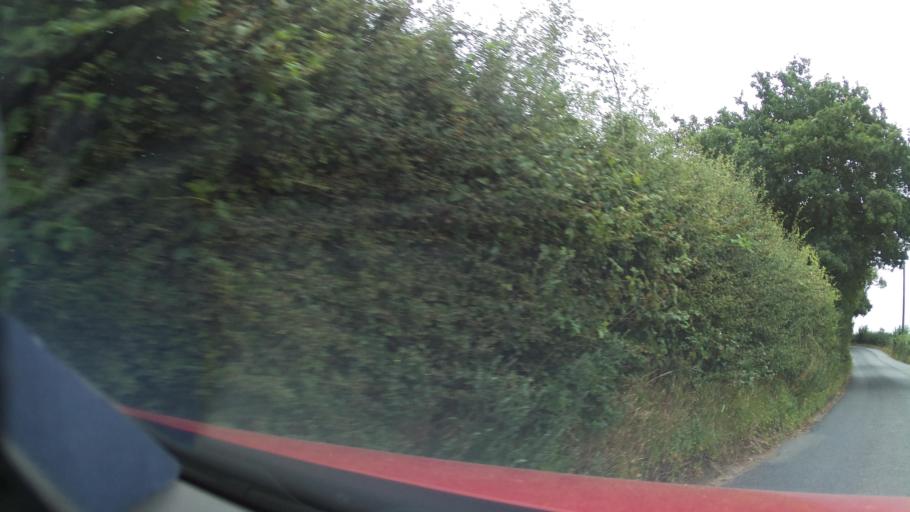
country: GB
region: England
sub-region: Derbyshire
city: Swadlincote
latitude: 52.7968
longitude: -1.5386
